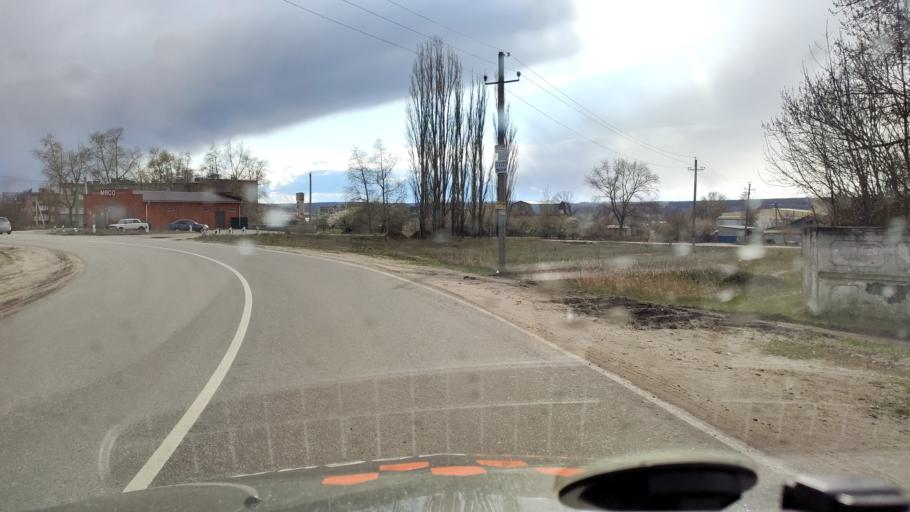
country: RU
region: Voronezj
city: Podgornoye
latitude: 51.8907
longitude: 39.1773
